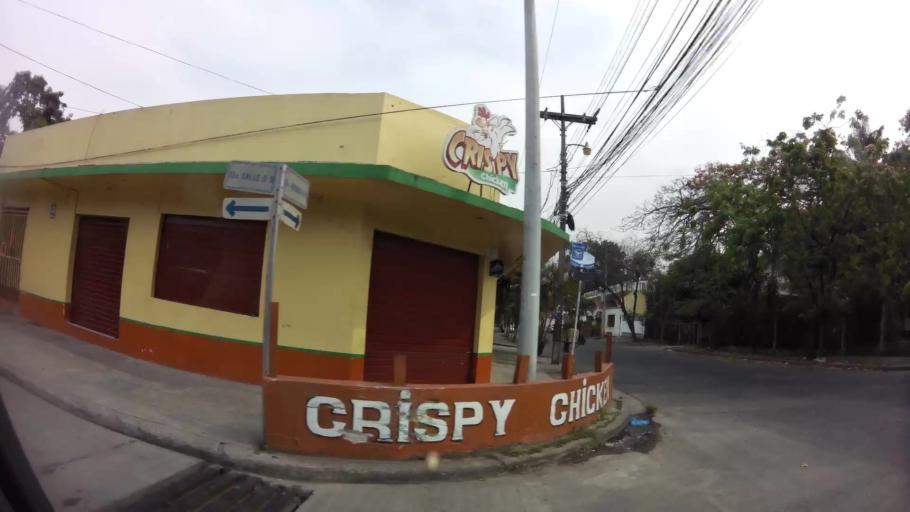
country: HN
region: Cortes
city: San Pedro Sula
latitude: 15.4953
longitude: -88.0307
